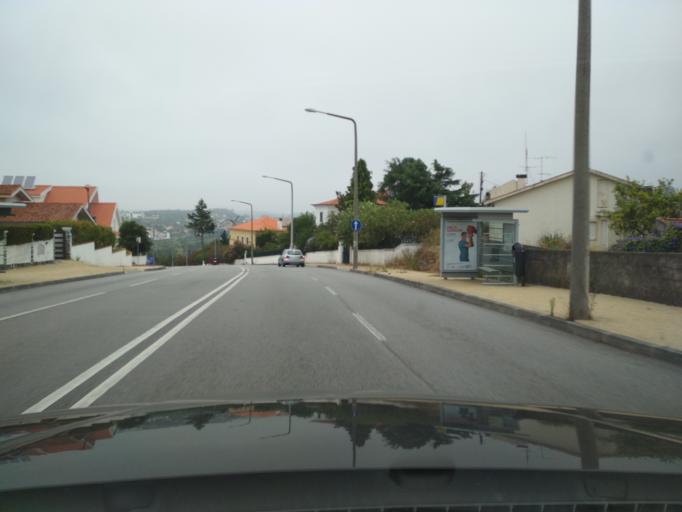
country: PT
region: Coimbra
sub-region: Coimbra
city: Coimbra
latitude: 40.2213
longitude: -8.4074
